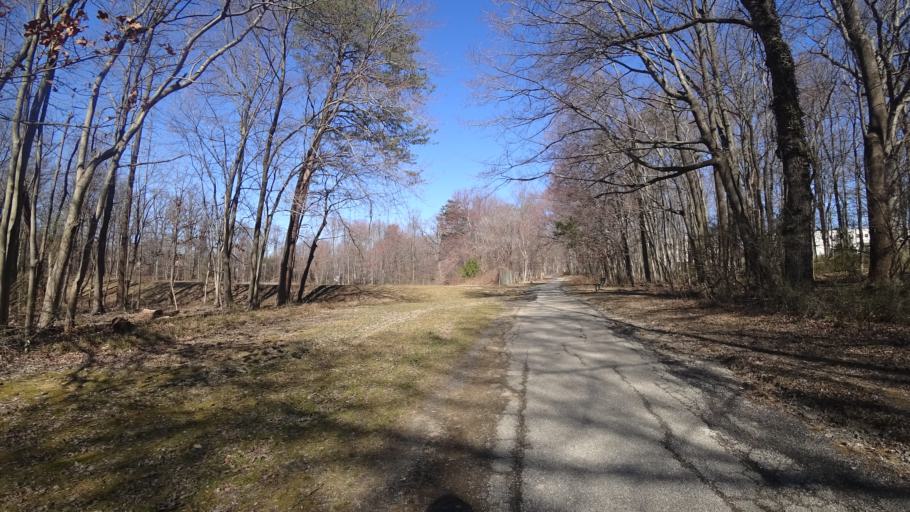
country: US
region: Maryland
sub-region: Montgomery County
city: Kemp Mill
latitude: 39.0385
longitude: -77.0315
